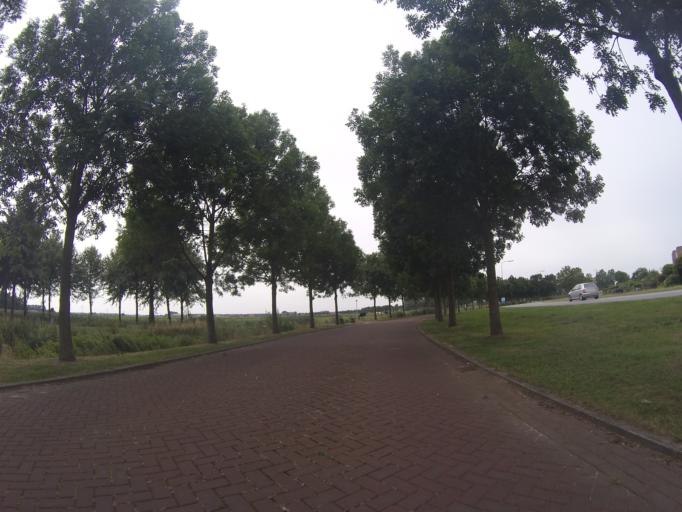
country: NL
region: Utrecht
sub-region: Gemeente Bunschoten
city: Bunschoten
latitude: 52.2434
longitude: 5.3831
